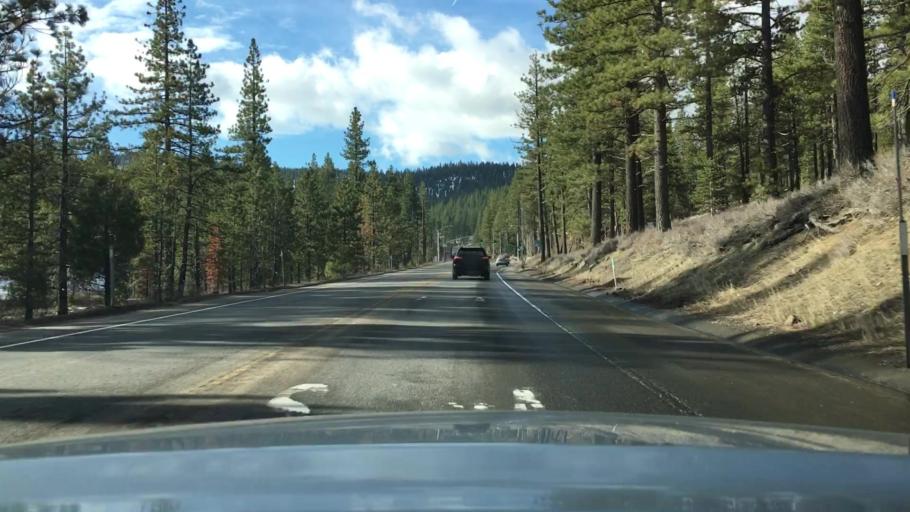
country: US
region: California
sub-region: Placer County
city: Tahoe Vista
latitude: 39.2895
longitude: -120.1035
